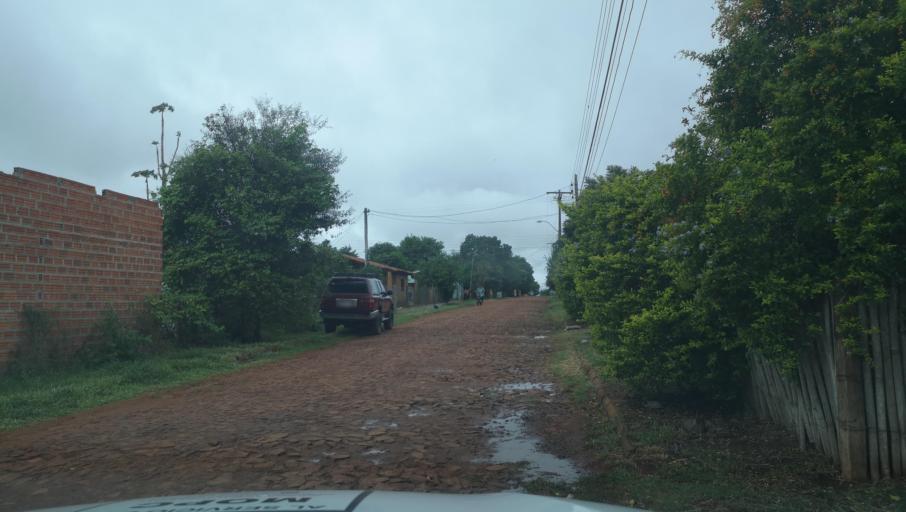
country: PY
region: Misiones
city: Santa Maria
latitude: -26.8974
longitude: -57.0367
